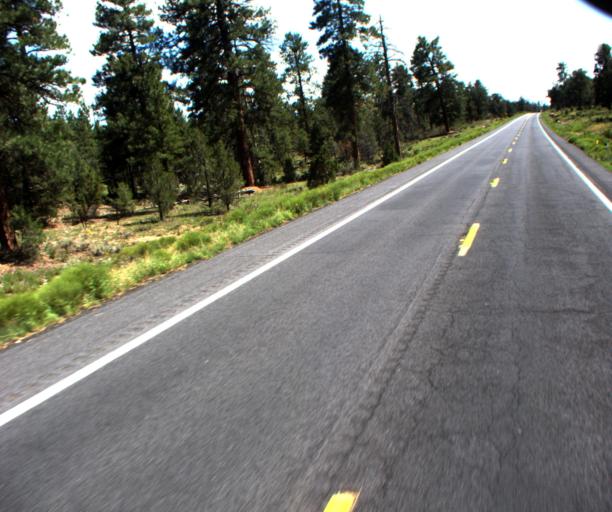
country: US
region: Arizona
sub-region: Coconino County
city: Grand Canyon Village
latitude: 35.9003
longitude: -112.1297
